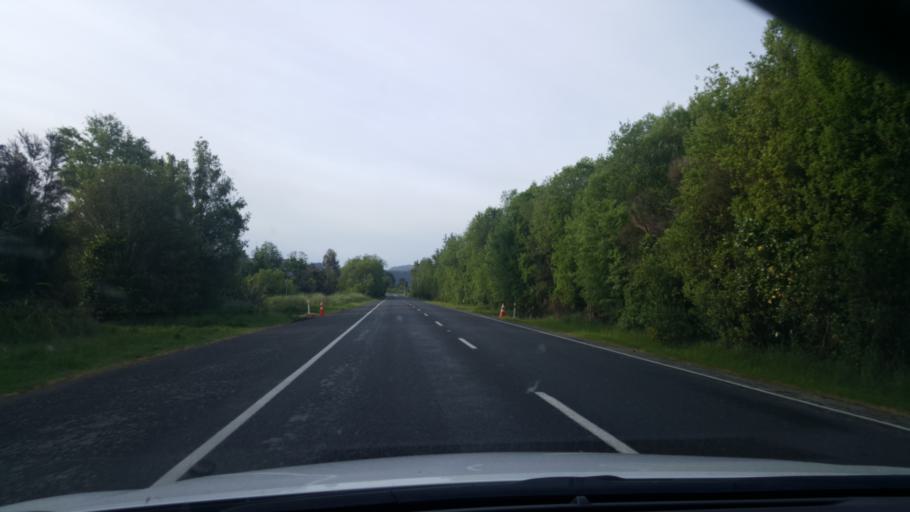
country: NZ
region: Waikato
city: Turangi
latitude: -38.9684
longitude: 175.7685
